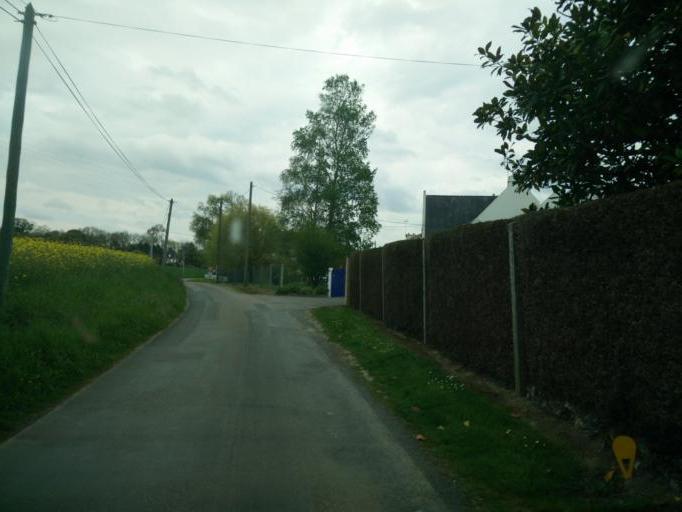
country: FR
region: Brittany
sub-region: Departement des Cotes-d'Armor
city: Yffiniac
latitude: 48.4934
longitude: -2.6738
